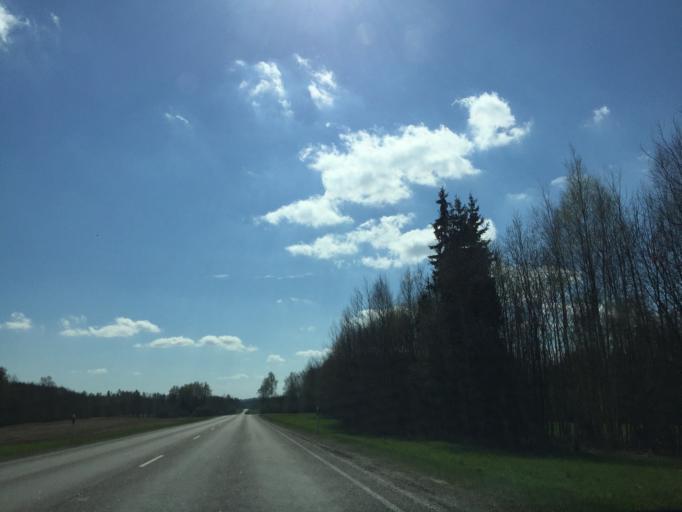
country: EE
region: Tartu
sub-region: Elva linn
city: Elva
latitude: 58.1044
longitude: 26.2351
